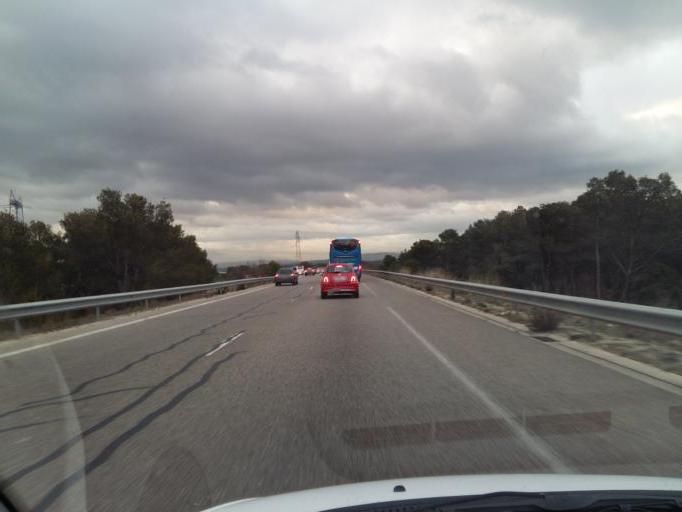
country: FR
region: Provence-Alpes-Cote d'Azur
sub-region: Departement des Bouches-du-Rhone
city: Les Pennes-Mirabeau
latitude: 43.4518
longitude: 5.3066
